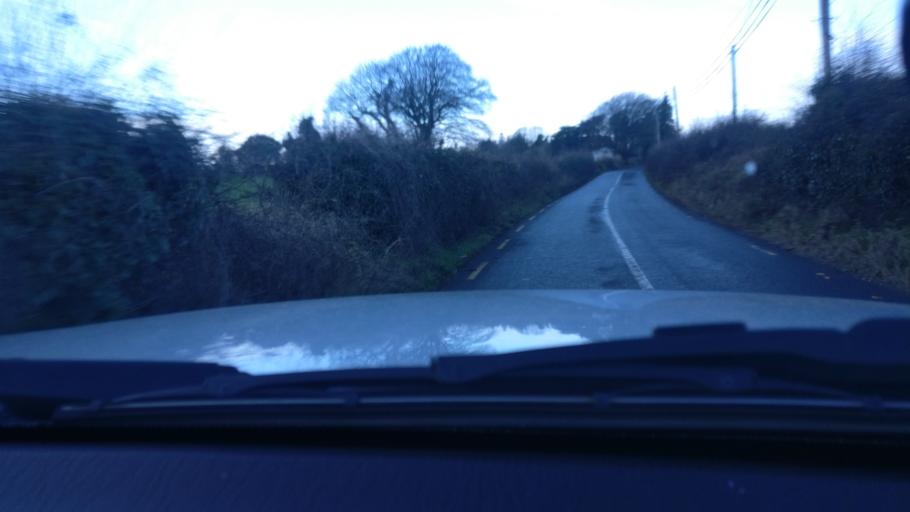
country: IE
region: Connaught
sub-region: County Galway
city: Loughrea
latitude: 53.2255
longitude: -8.4079
